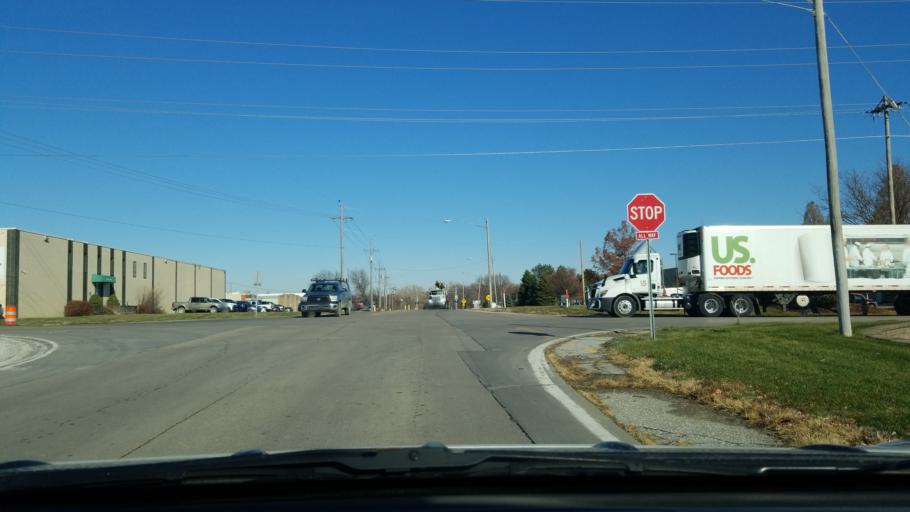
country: US
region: Nebraska
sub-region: Douglas County
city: Ralston
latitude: 41.2160
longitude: -96.0719
